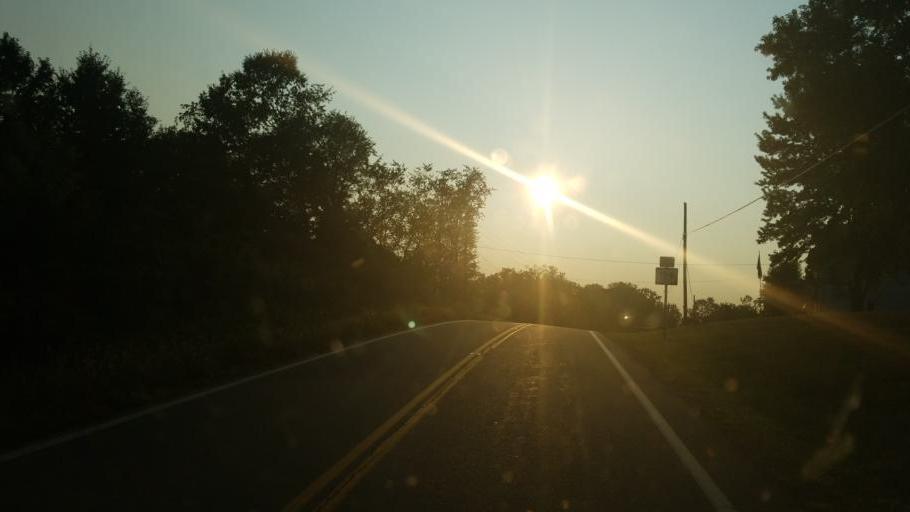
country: US
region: Ohio
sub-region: Ashland County
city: Loudonville
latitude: 40.6574
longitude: -82.1327
